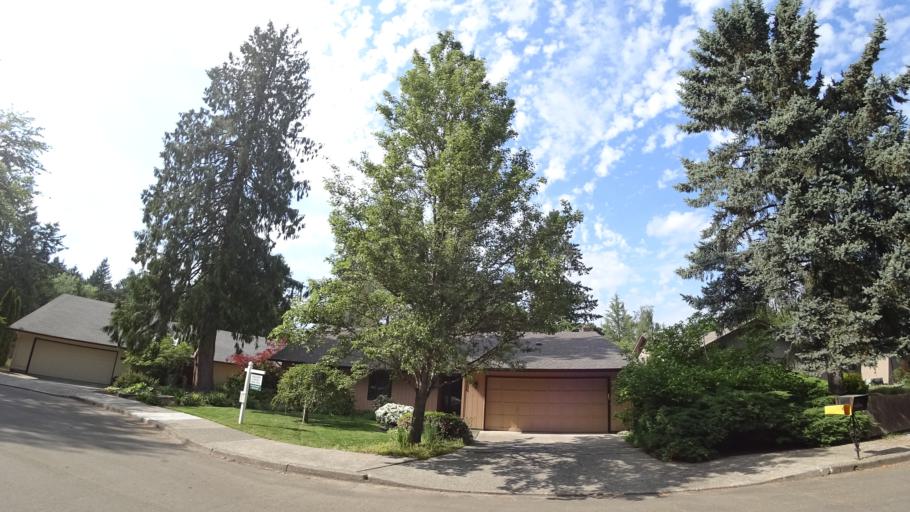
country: US
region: Oregon
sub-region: Washington County
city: Garden Home-Whitford
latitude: 45.4581
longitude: -122.7515
